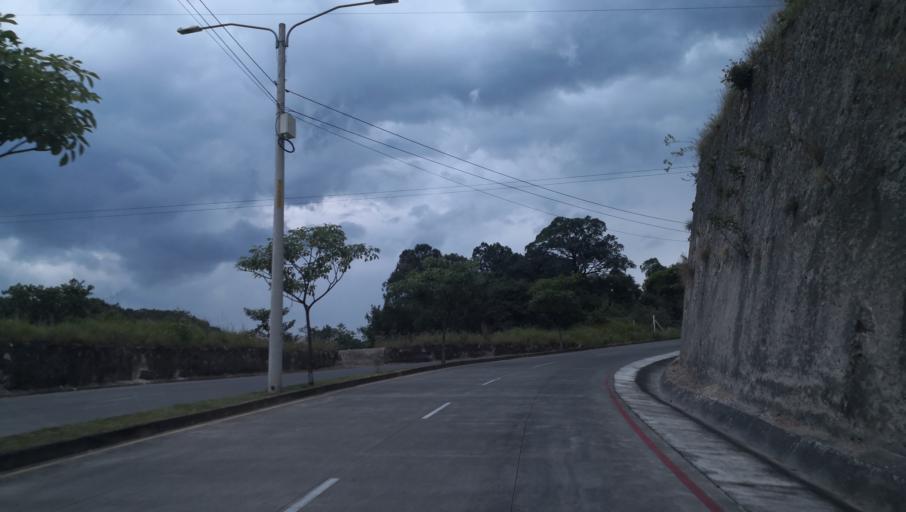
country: GT
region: Guatemala
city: Villa Nueva
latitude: 14.5546
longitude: -90.5951
